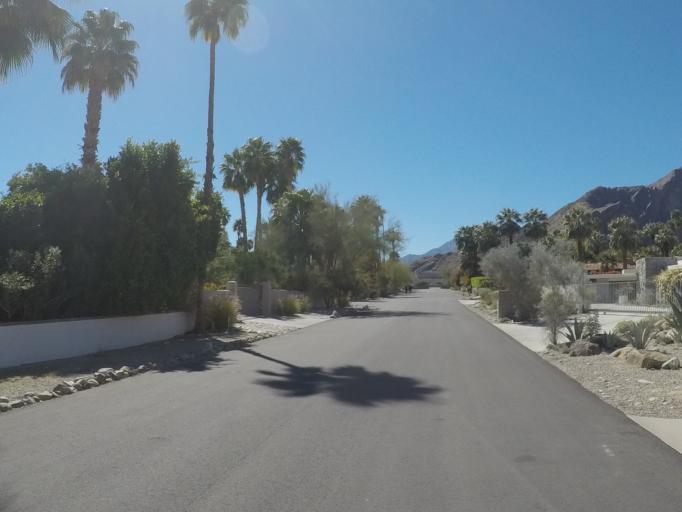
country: US
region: California
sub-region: Riverside County
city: Palm Springs
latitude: 33.8181
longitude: -116.5513
